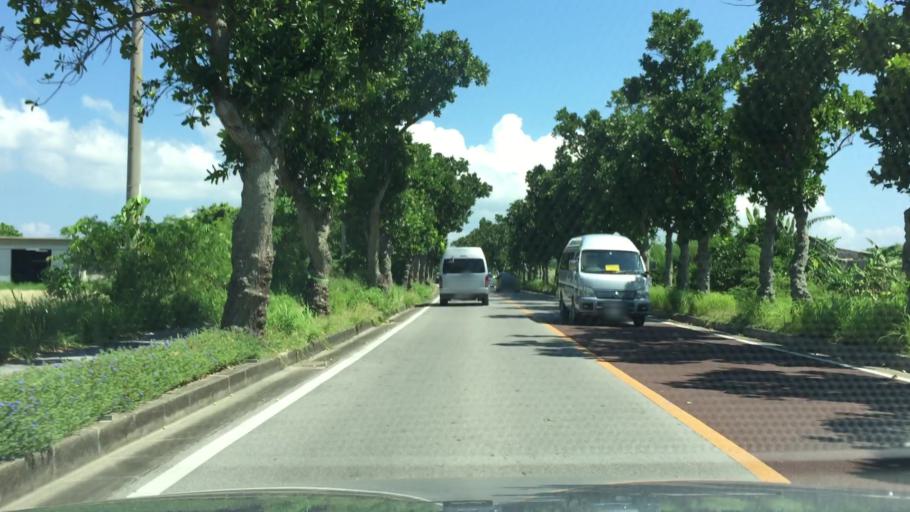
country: JP
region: Okinawa
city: Ishigaki
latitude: 24.3684
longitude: 124.2464
